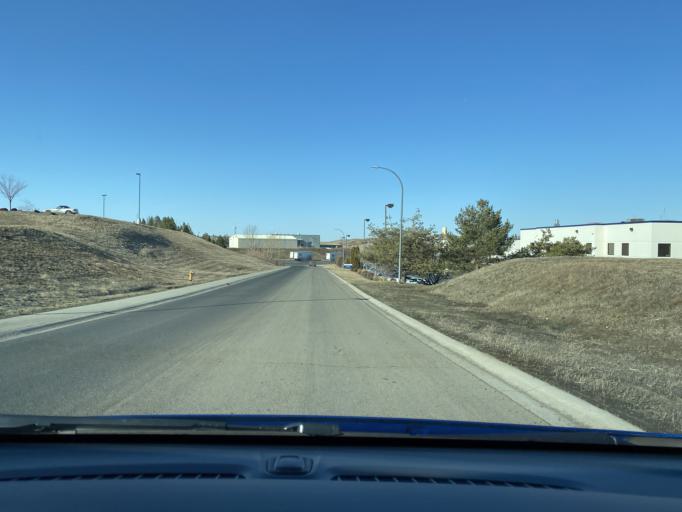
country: US
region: Washington
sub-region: Whitman County
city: Pullman
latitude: 46.7523
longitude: -117.1586
